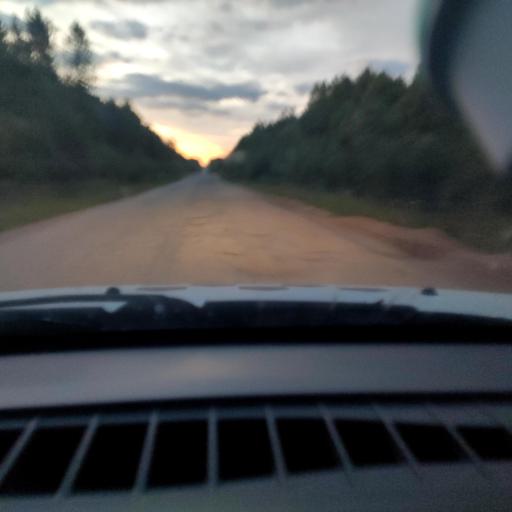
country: RU
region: Kirov
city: Darovskoy
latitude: 59.0016
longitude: 47.8754
